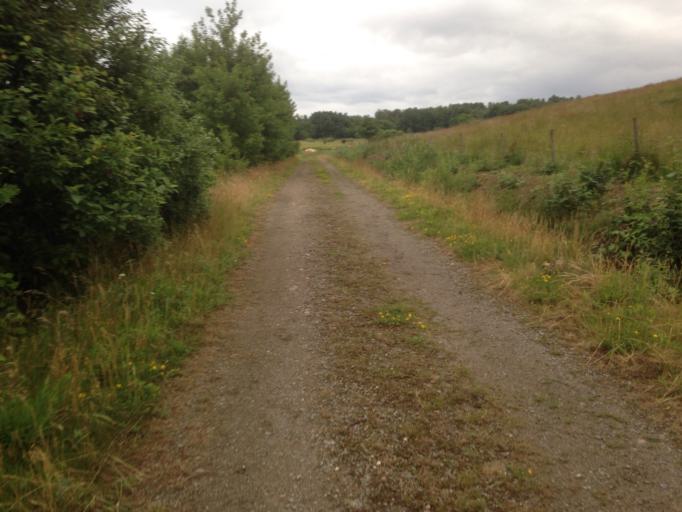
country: SE
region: Vaestra Goetaland
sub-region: Goteborg
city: Majorna
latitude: 57.7998
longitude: 11.8967
